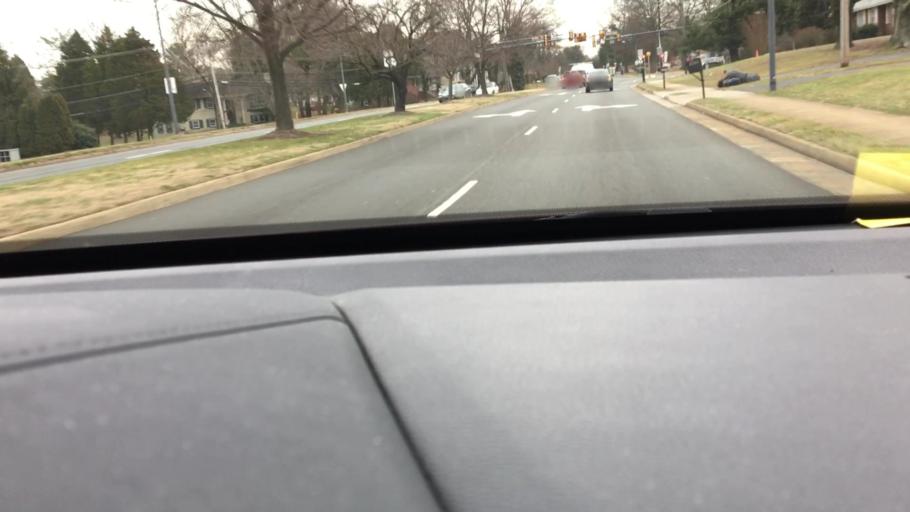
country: US
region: Virginia
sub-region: City of Manassas
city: Manassas
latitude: 38.7630
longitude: -77.4785
